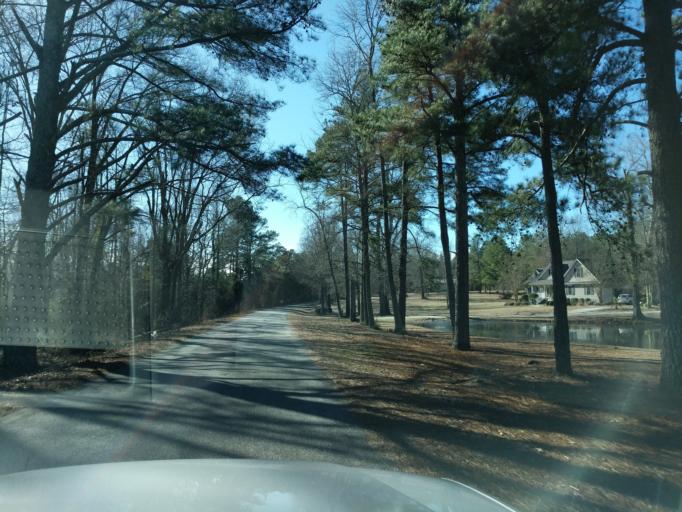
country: US
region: South Carolina
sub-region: Saluda County
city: Saluda
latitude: 34.0473
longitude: -81.8234
